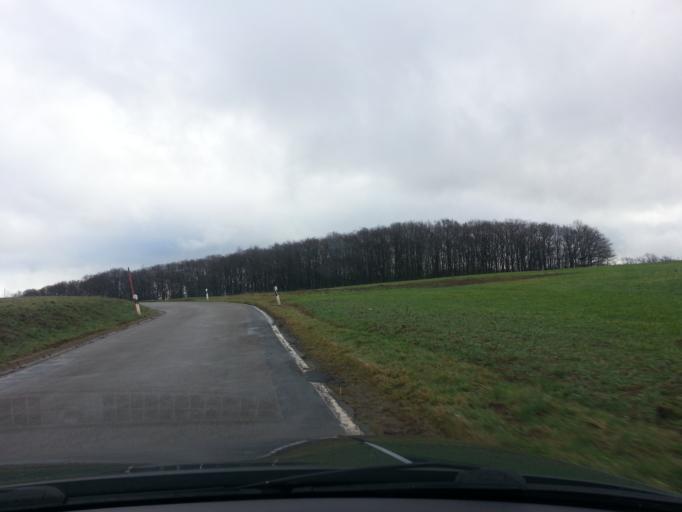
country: DE
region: Rheinland-Pfalz
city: Neunkirchen am Potzberg
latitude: 49.4831
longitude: 7.4921
